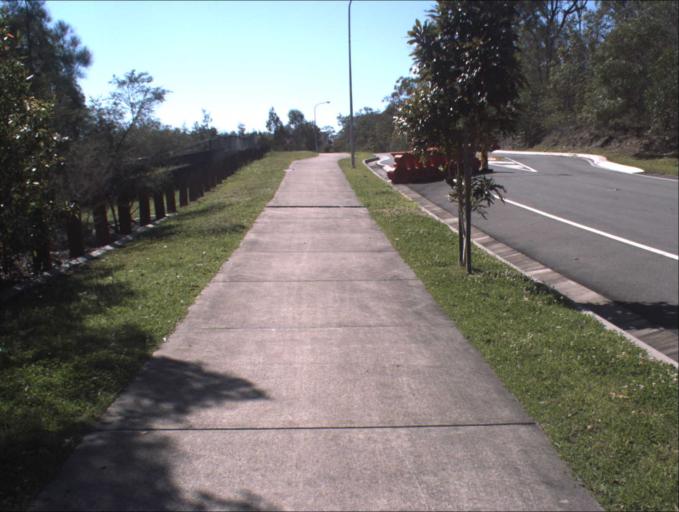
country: AU
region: Queensland
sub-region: Logan
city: Windaroo
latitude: -27.7225
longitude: 153.1688
